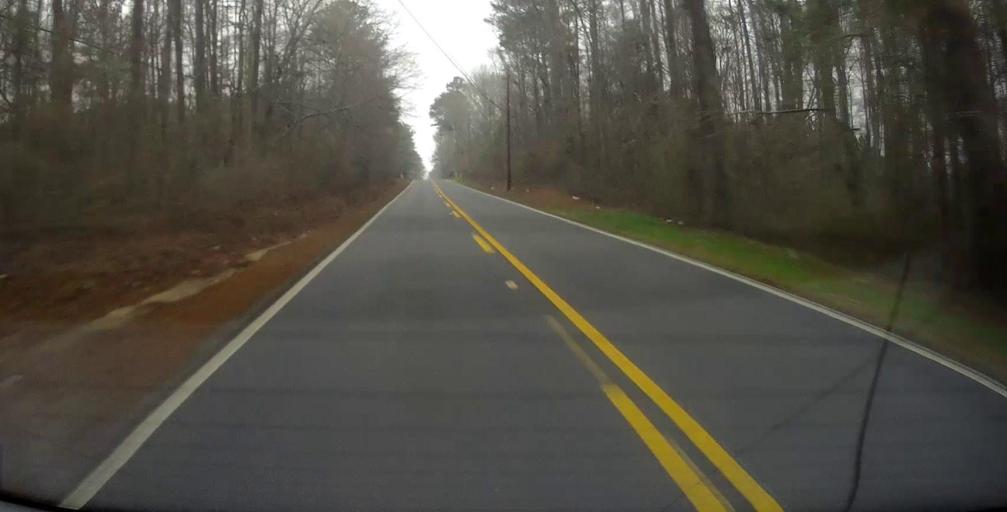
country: US
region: Georgia
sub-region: Spalding County
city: East Griffin
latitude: 33.2107
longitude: -84.2312
